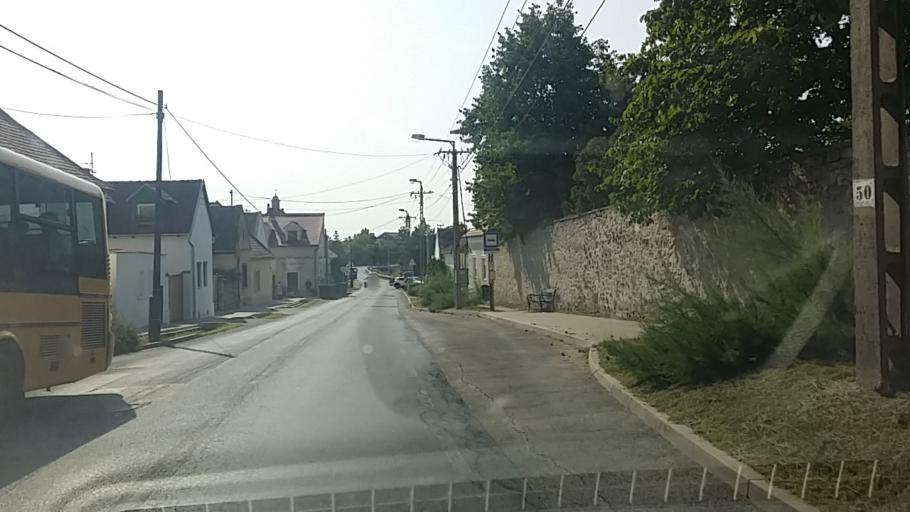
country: HU
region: Gyor-Moson-Sopron
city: Fertorakos
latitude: 47.7168
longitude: 16.6537
